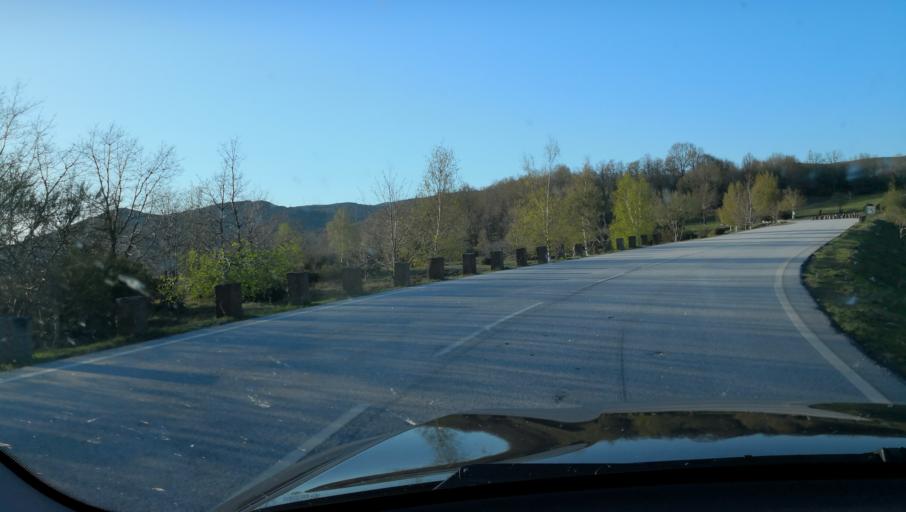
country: PT
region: Vila Real
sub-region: Vila Real
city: Vila Real
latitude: 41.3700
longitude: -7.8023
